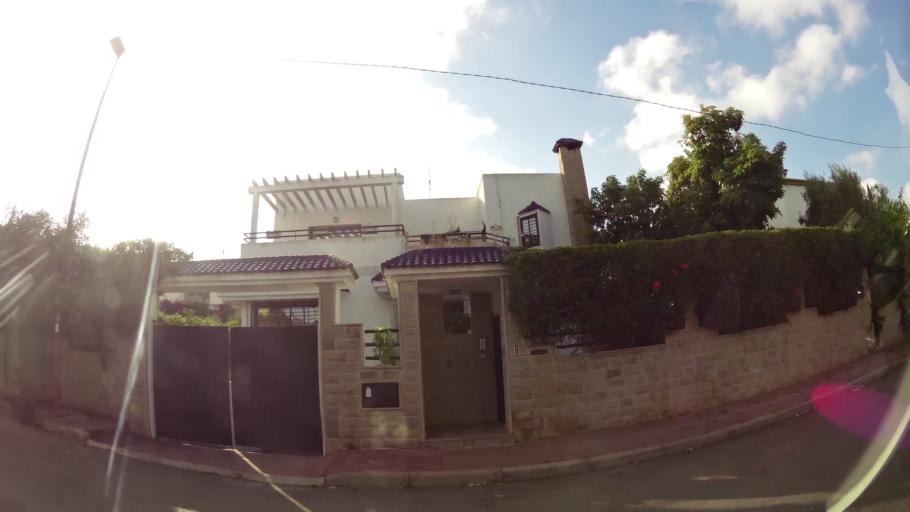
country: MA
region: Rabat-Sale-Zemmour-Zaer
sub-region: Skhirate-Temara
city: Temara
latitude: 33.9561
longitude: -6.8601
